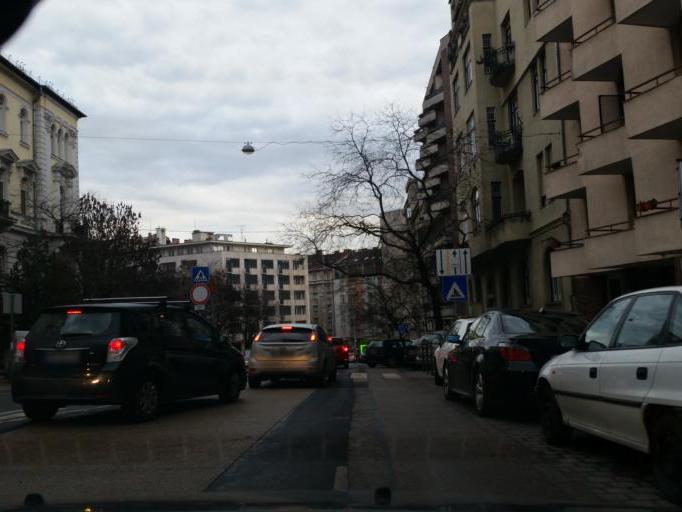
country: HU
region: Budapest
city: Budapest II. keruelet
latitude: 47.5118
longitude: 19.0304
